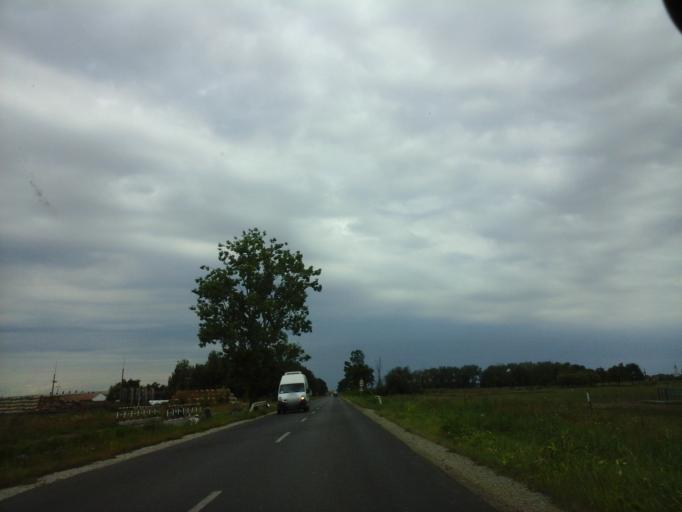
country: HU
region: Hajdu-Bihar
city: Balmazujvaros
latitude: 47.5903
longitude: 21.3433
